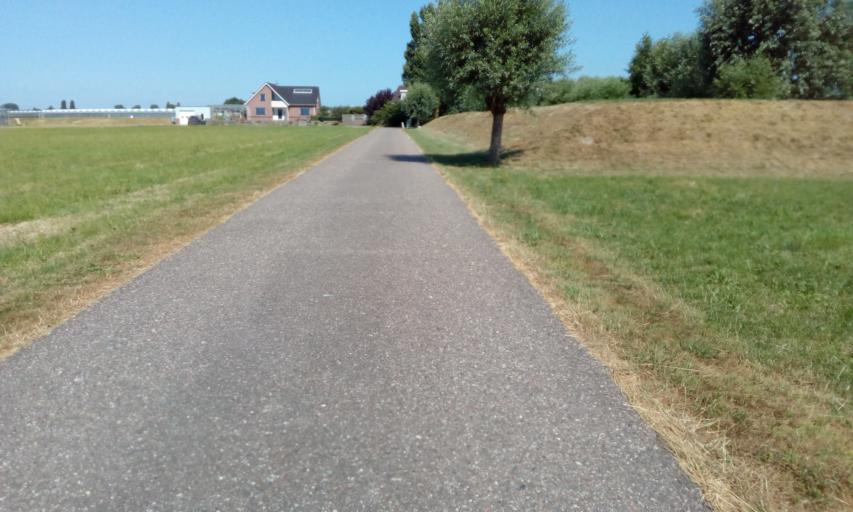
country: NL
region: South Holland
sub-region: Gemeente Westland
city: De Lier
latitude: 51.9796
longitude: 4.2964
